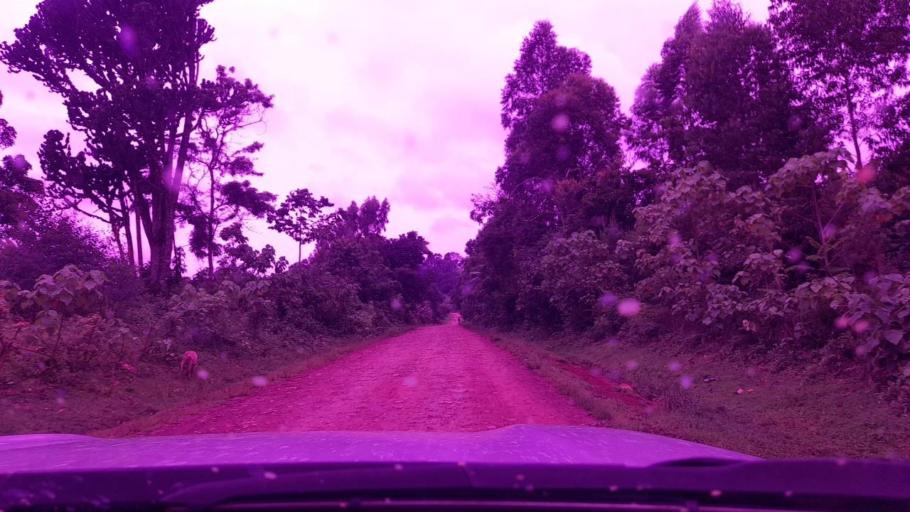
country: ET
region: Southern Nations, Nationalities, and People's Region
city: Bonga
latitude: 7.5516
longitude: 35.8528
